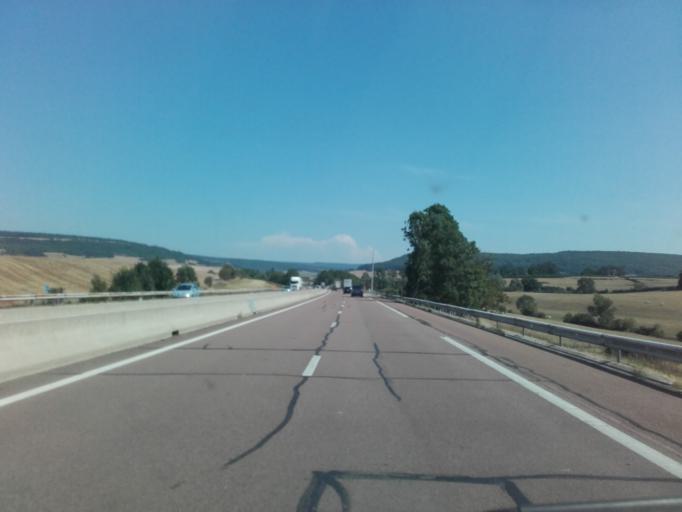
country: FR
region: Bourgogne
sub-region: Departement de la Cote-d'Or
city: Pouilly-en-Auxois
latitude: 47.2114
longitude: 4.6124
